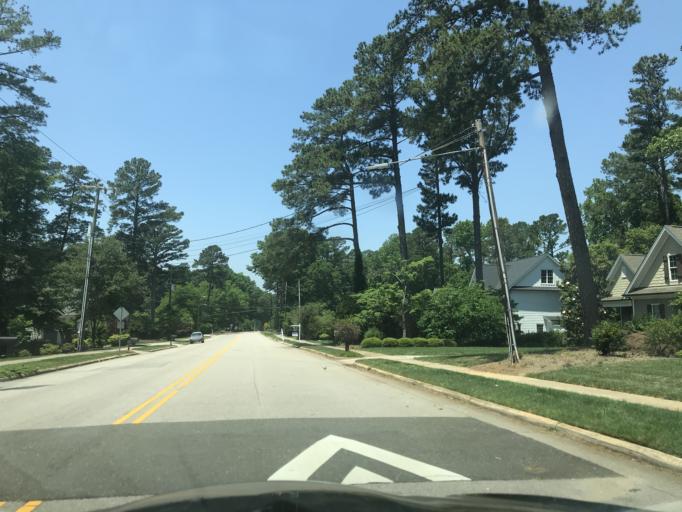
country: US
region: North Carolina
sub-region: Wake County
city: West Raleigh
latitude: 35.8516
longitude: -78.6497
